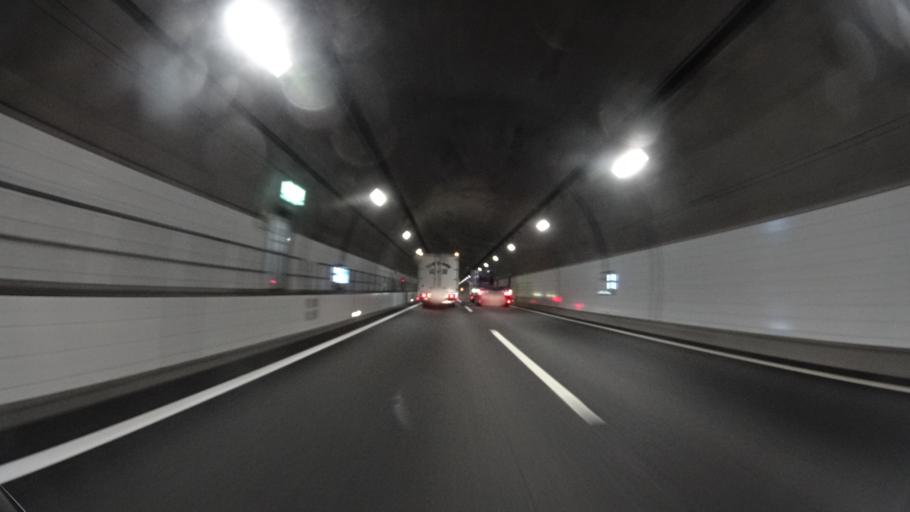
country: JP
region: Tochigi
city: Tanuma
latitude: 36.3511
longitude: 139.6025
